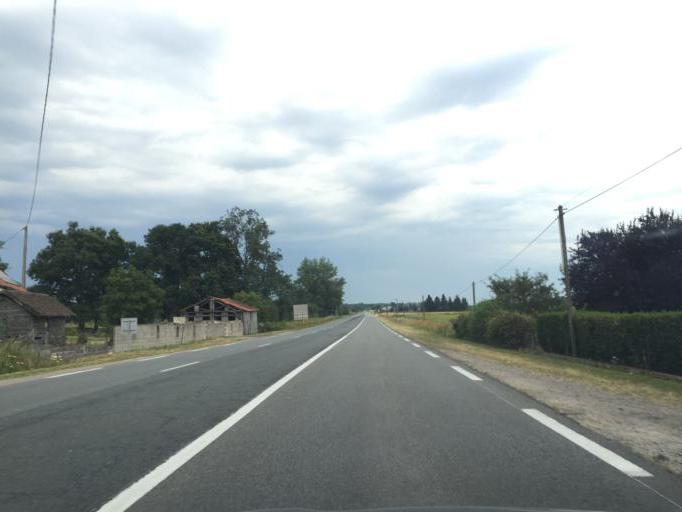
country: FR
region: Auvergne
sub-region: Departement de l'Allier
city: Varennes-sur-Allier
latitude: 46.3660
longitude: 3.3667
